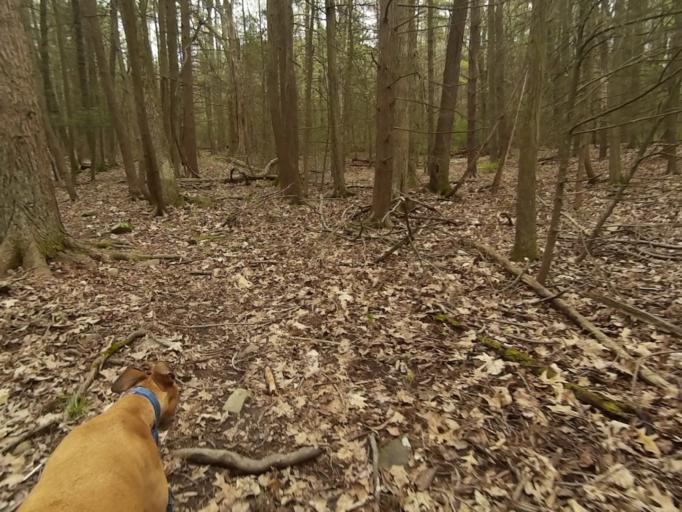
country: US
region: Pennsylvania
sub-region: Centre County
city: Boalsburg
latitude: 40.7561
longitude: -77.8205
